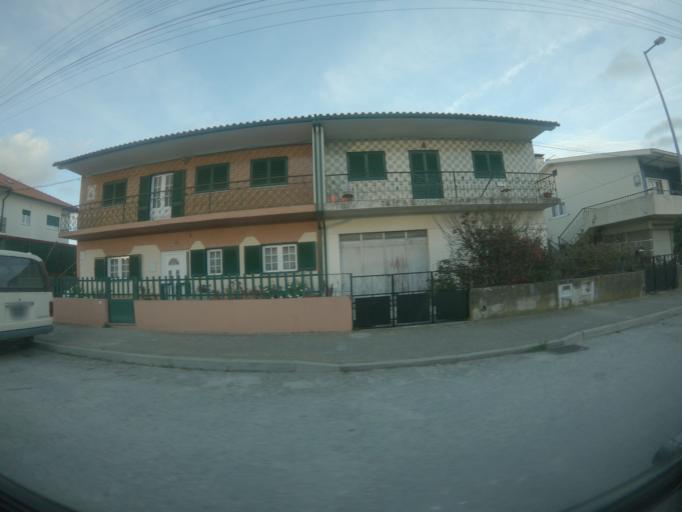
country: PT
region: Braganca
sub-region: Carrazeda de Ansiaes
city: Carrazeda de Anciaes
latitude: 41.2392
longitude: -7.3056
